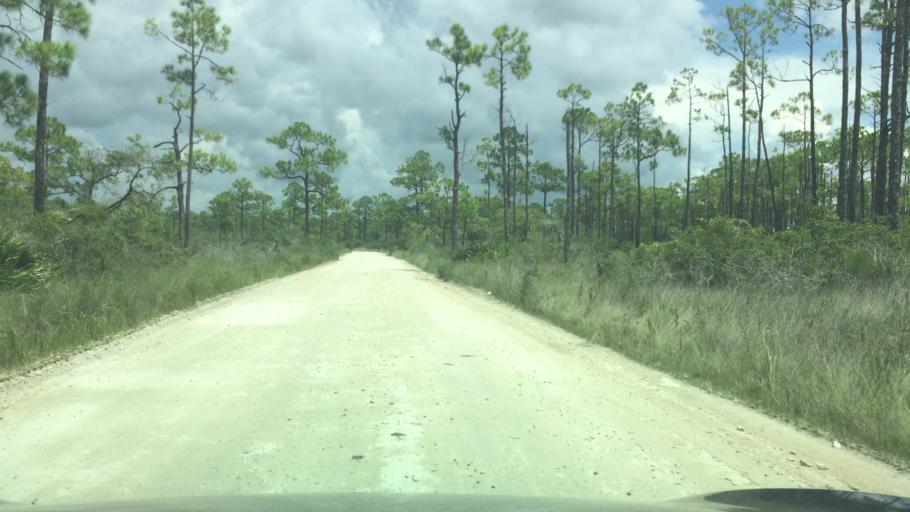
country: US
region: Florida
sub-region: Bay County
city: Mexico Beach
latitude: 29.9617
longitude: -85.4524
